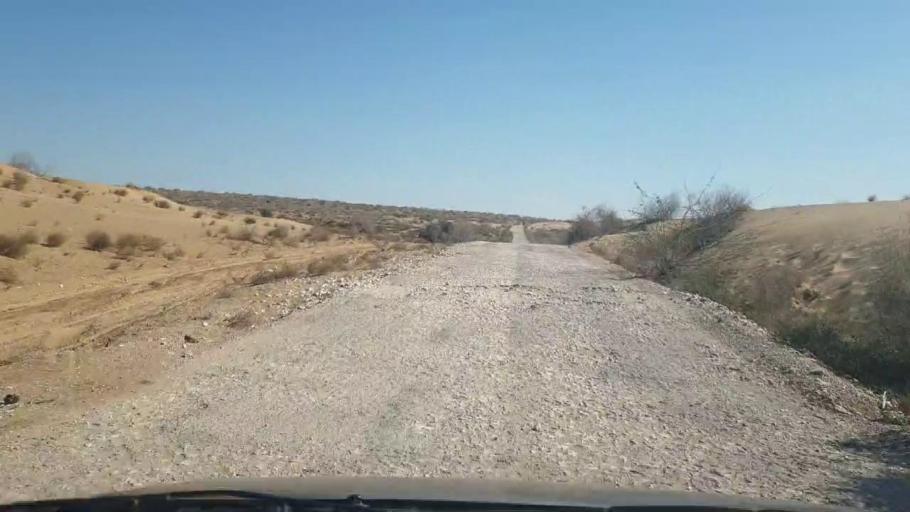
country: PK
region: Sindh
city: Bozdar
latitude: 27.0192
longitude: 68.7295
